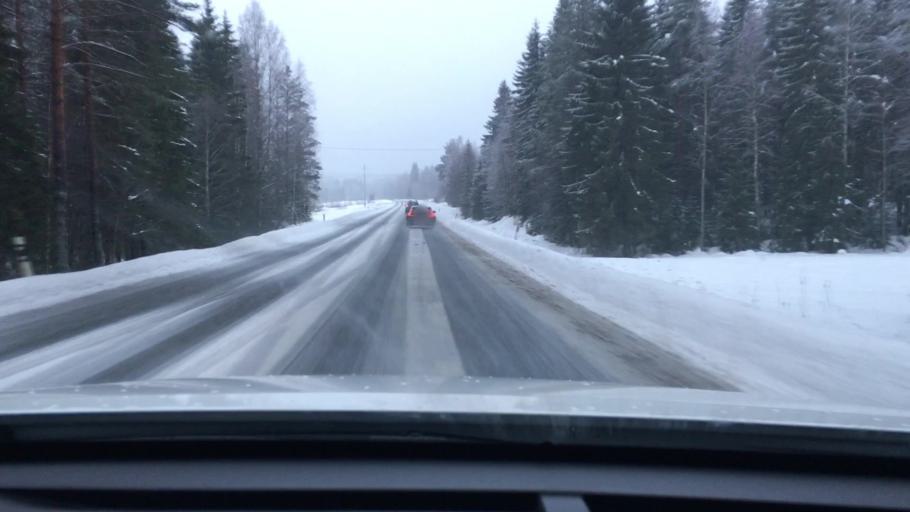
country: FI
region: Northern Savo
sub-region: Ylae-Savo
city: Sonkajaervi
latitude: 63.7611
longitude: 27.4033
